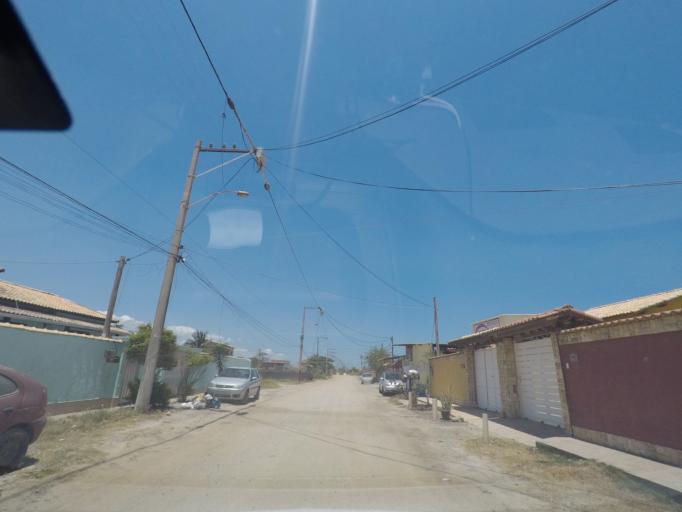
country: BR
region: Rio de Janeiro
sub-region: Marica
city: Marica
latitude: -22.9690
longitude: -42.9637
